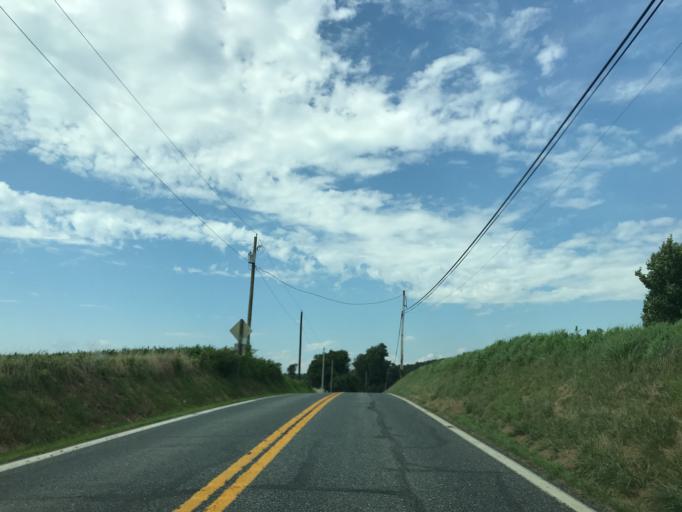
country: US
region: Pennsylvania
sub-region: York County
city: Susquehanna Trails
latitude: 39.6819
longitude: -76.4097
